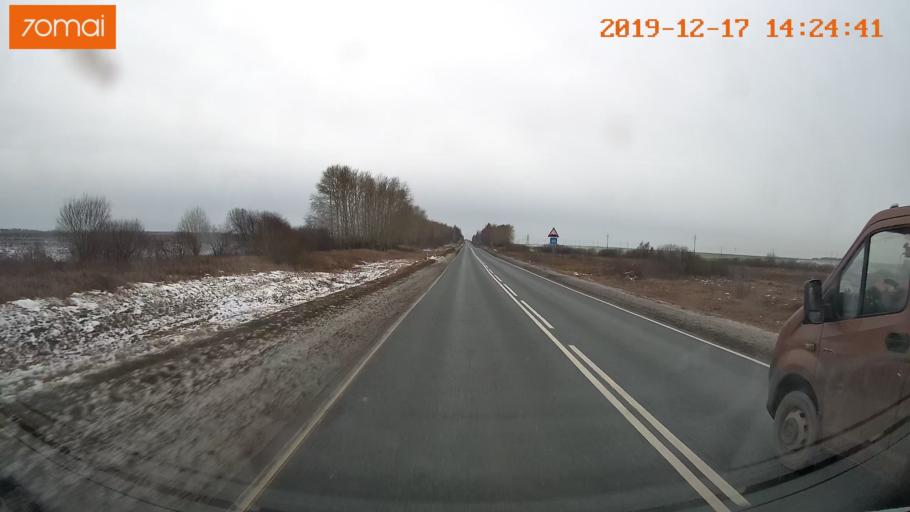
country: RU
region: Rjazan
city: Zakharovo
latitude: 54.3987
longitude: 39.3465
